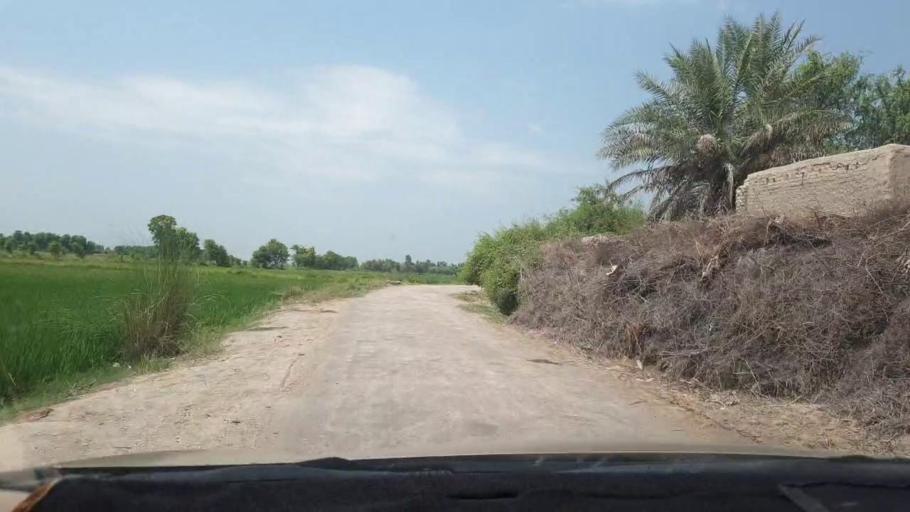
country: PK
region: Sindh
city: Naudero
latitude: 27.7336
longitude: 68.3489
